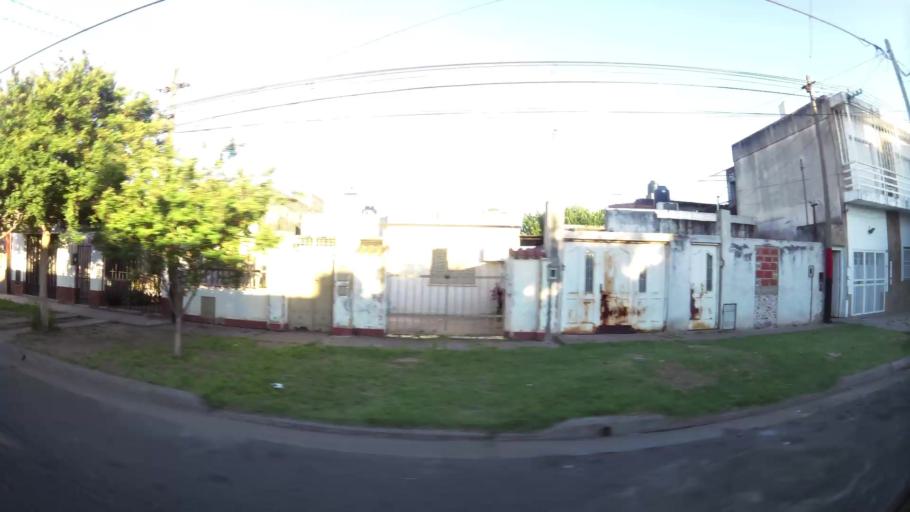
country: AR
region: Santa Fe
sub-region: Departamento de Rosario
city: Rosario
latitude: -32.9730
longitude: -60.6713
